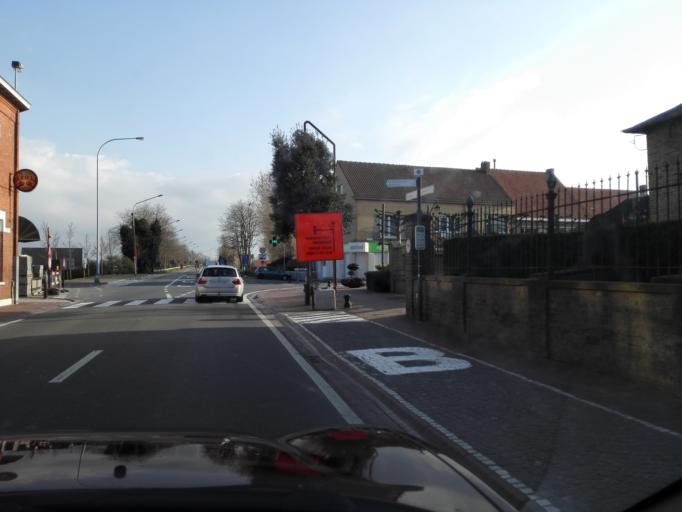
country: BE
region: Flanders
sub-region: Provincie West-Vlaanderen
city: De Panne
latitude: 51.0754
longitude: 2.6034
